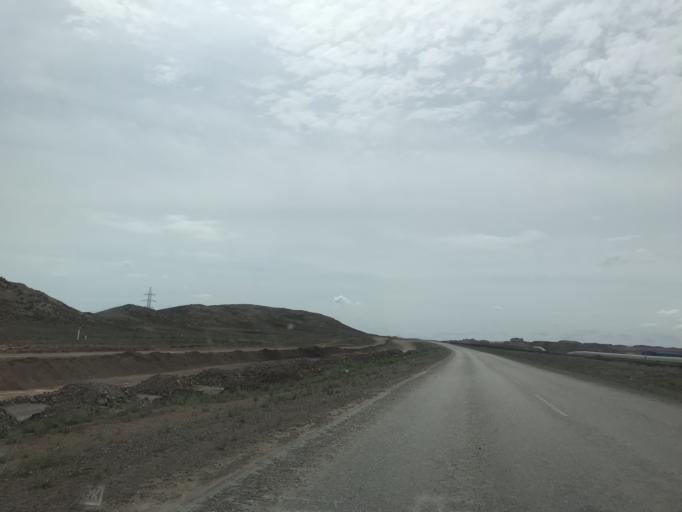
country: KZ
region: Zhambyl
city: Mynaral
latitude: 45.3727
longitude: 73.6570
